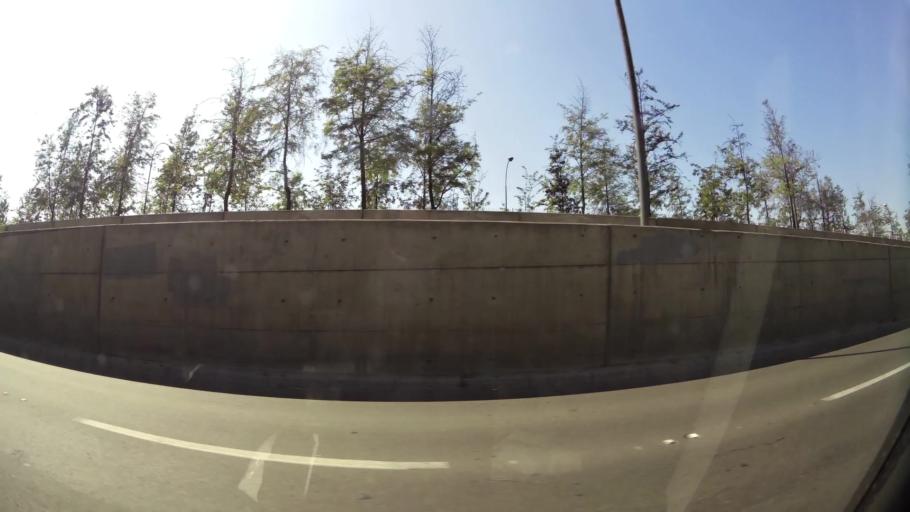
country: CL
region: Santiago Metropolitan
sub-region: Provincia de Santiago
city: Santiago
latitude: -33.4643
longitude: -70.6569
